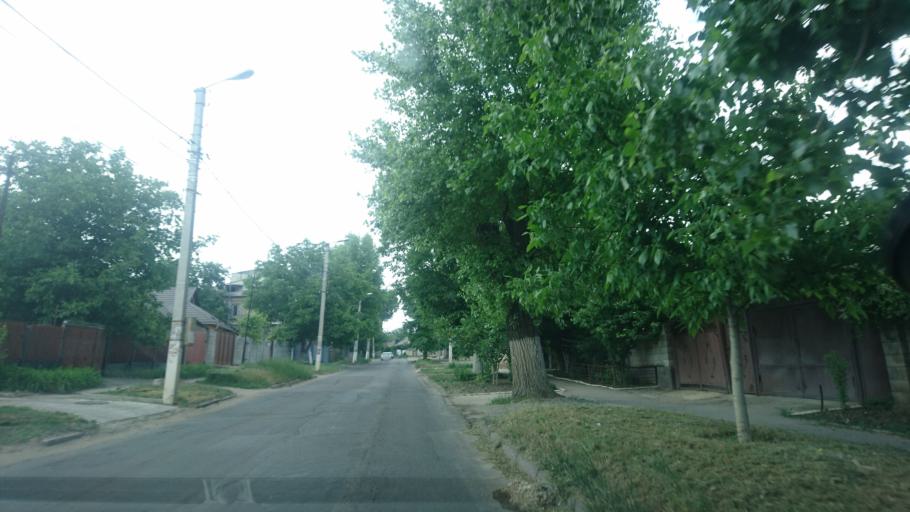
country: MD
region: Chisinau
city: Chisinau
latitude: 47.0526
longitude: 28.8422
